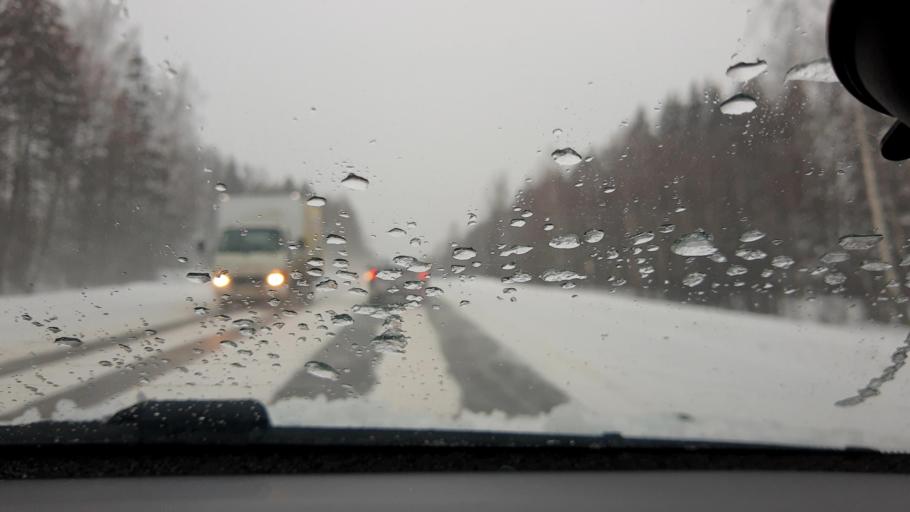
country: RU
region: Nizjnij Novgorod
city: Pervomayskiy
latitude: 56.6279
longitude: 43.2286
